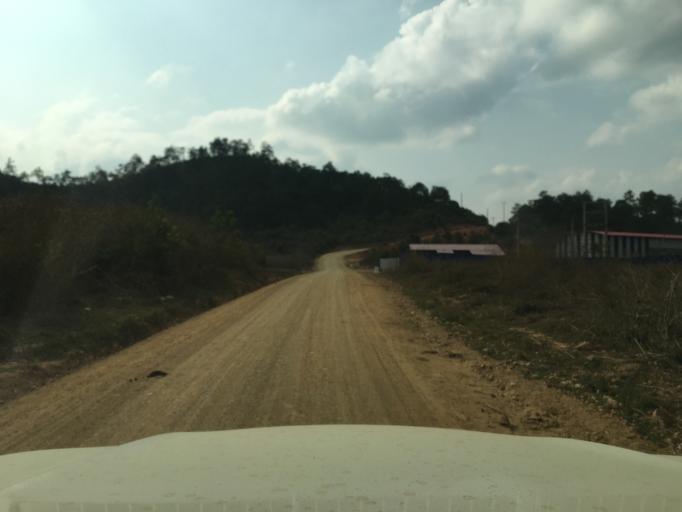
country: LA
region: Houaphan
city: Huameung
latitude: 20.2087
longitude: 103.8738
